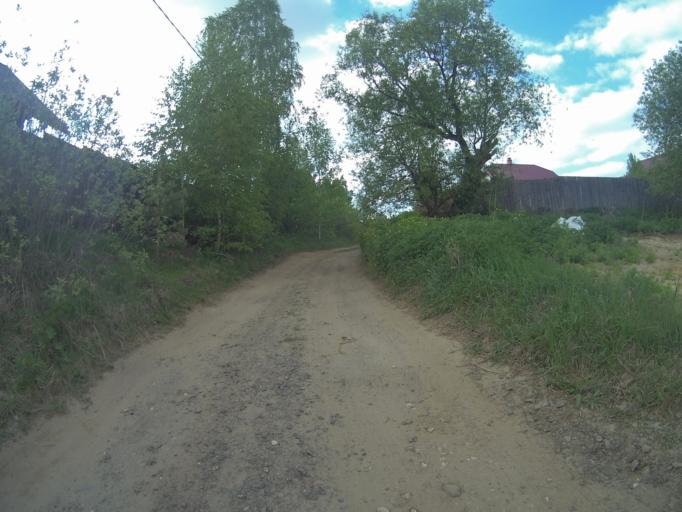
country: RU
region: Vladimir
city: Raduzhnyy
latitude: 55.9950
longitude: 40.2309
